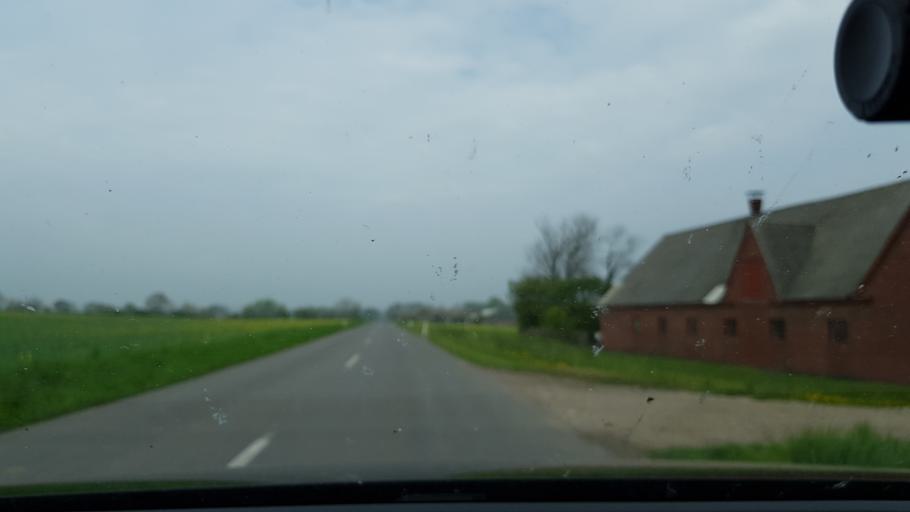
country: DK
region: Capital Region
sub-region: Bornholm Kommune
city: Nexo
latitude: 55.0109
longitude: 15.0957
